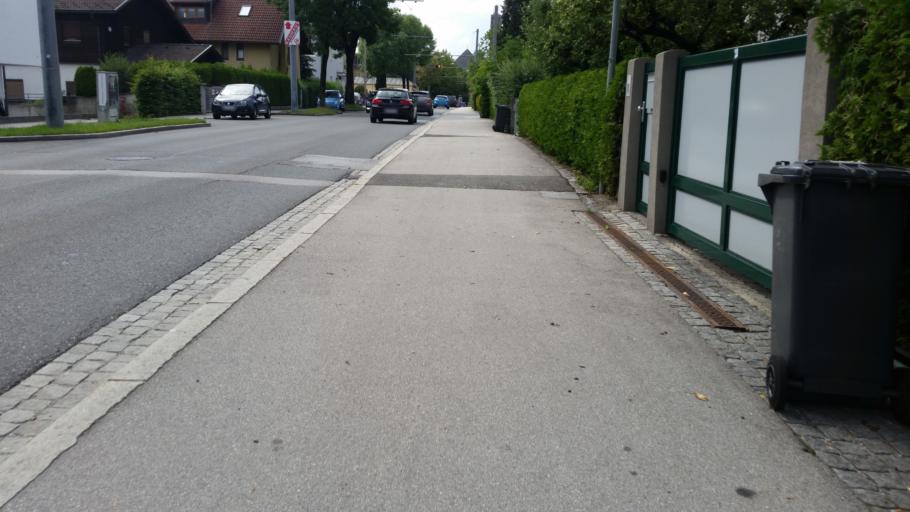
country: AT
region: Salzburg
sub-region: Politischer Bezirk Salzburg-Umgebung
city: Bergheim
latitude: 47.8099
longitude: 13.0102
